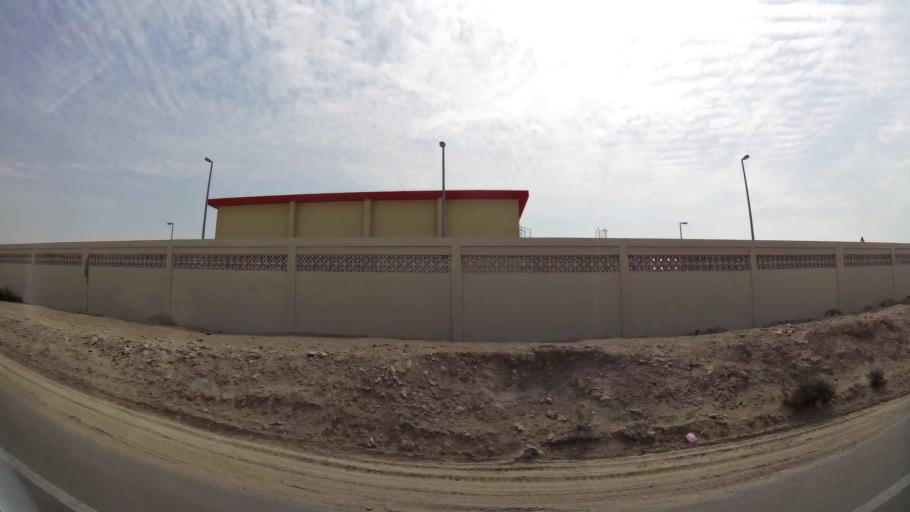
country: AE
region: Abu Dhabi
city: Abu Dhabi
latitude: 24.5643
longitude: 54.6794
